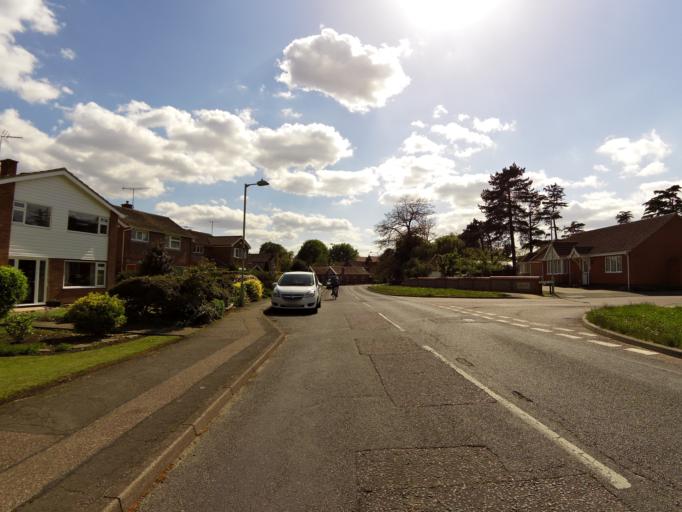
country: GB
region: England
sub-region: Suffolk
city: Kessingland
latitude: 52.4528
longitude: 1.6946
